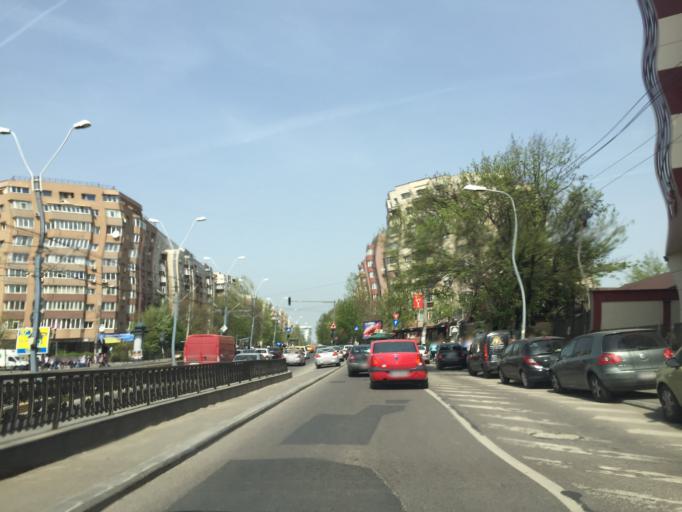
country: RO
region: Ilfov
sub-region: Comuna Chiajna
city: Rosu
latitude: 44.4357
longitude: 26.0353
